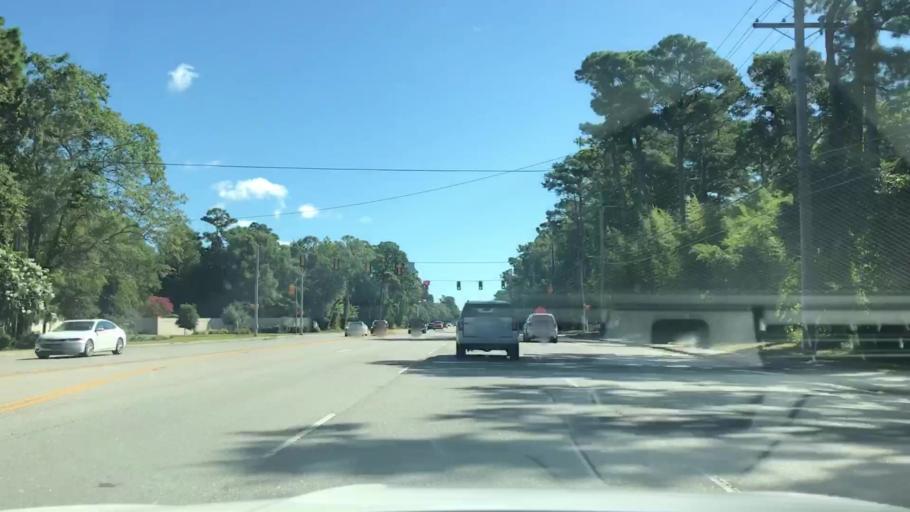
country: US
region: South Carolina
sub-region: Horry County
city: North Myrtle Beach
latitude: 33.7932
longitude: -78.7562
